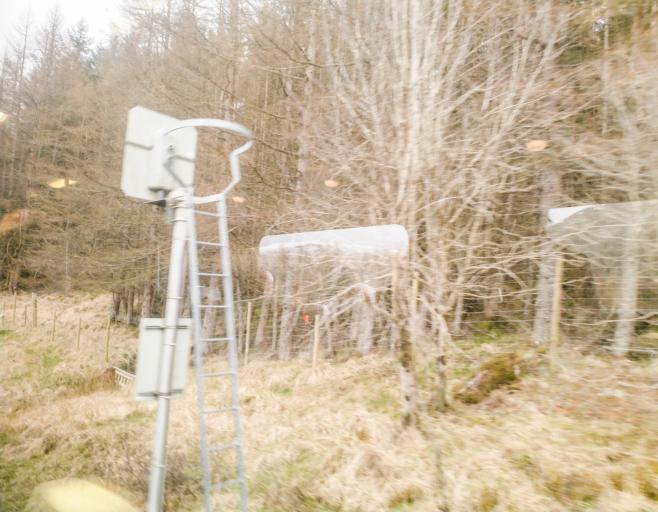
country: GB
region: Scotland
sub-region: Argyll and Bute
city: Garelochhead
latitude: 56.4365
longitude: -4.7053
